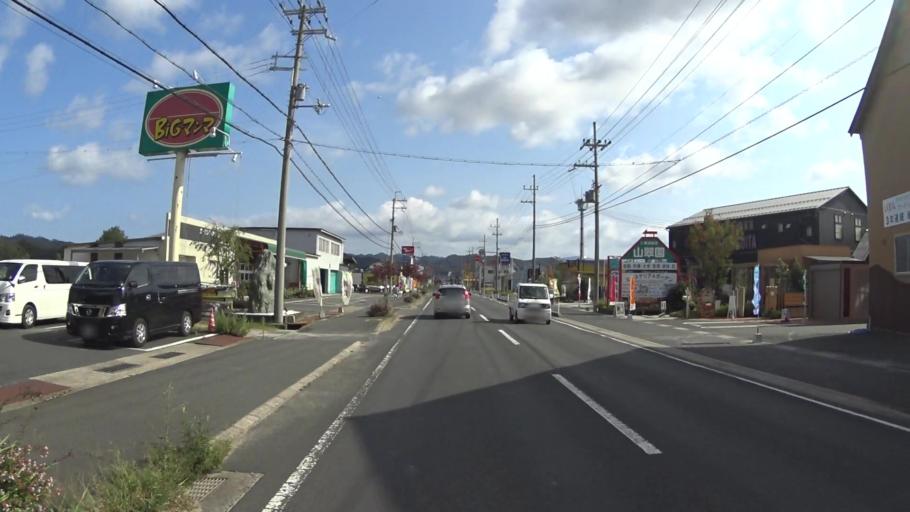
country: JP
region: Kyoto
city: Miyazu
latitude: 35.5982
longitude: 135.0885
